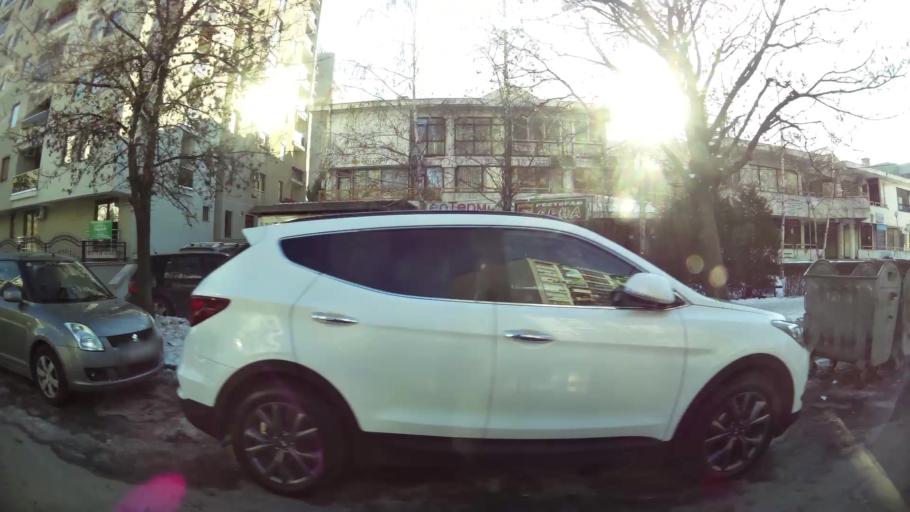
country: MK
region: Karpos
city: Skopje
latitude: 42.0049
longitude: 21.3937
